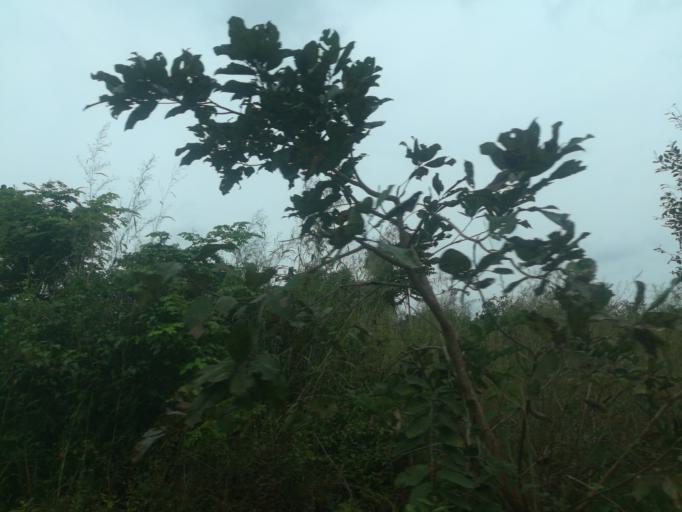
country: NG
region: Ogun
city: Itori
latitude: 7.1020
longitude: 3.1522
